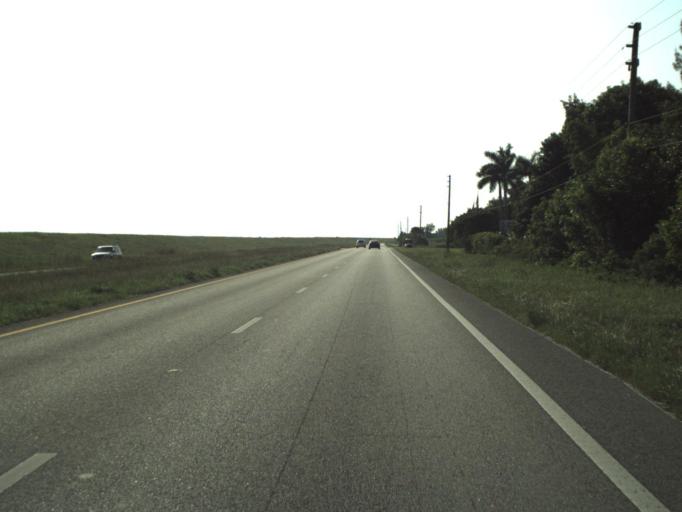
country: US
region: Florida
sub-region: Hendry County
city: Clewiston
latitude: 26.7407
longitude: -80.8798
